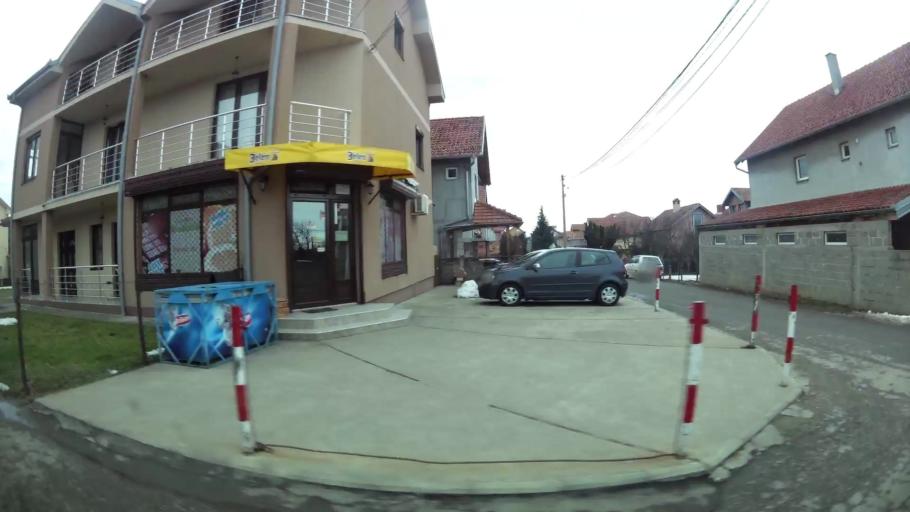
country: RS
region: Central Serbia
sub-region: Belgrade
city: Rakovica
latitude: 44.7414
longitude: 20.3972
